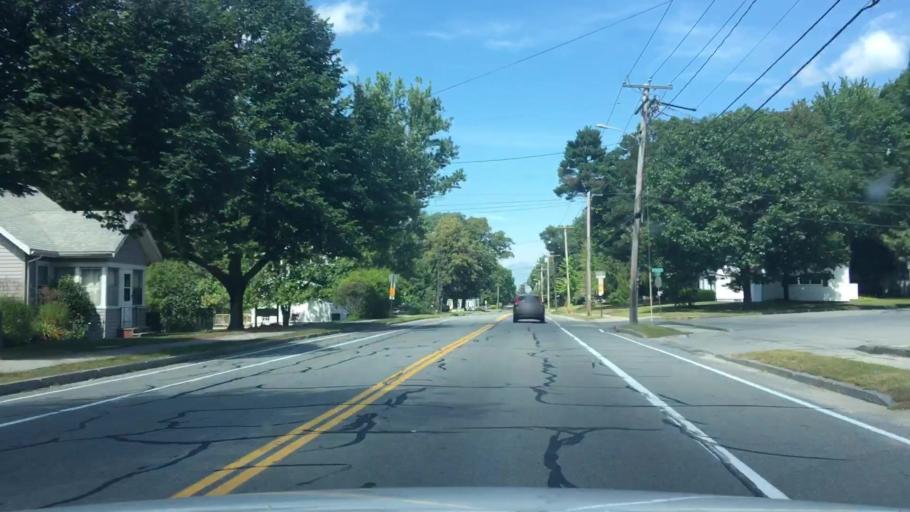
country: US
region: Maine
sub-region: Cumberland County
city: Falmouth
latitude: 43.7131
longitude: -70.2917
